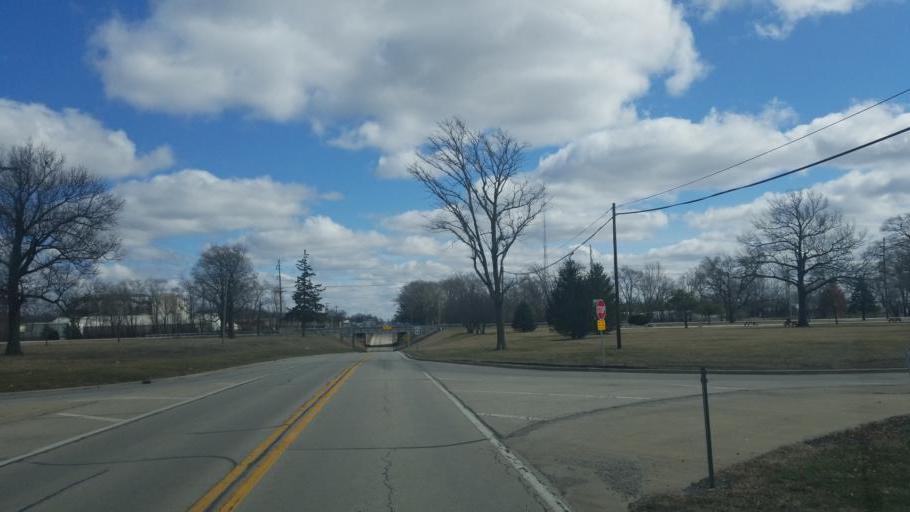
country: US
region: Illinois
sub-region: Douglas County
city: Tuscola
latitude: 39.7917
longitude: -88.2948
